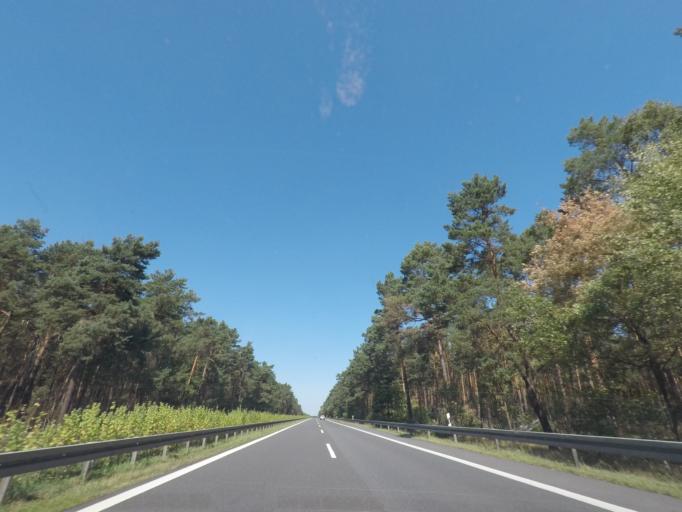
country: DE
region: Brandenburg
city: Bronkow
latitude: 51.7242
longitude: 13.8805
